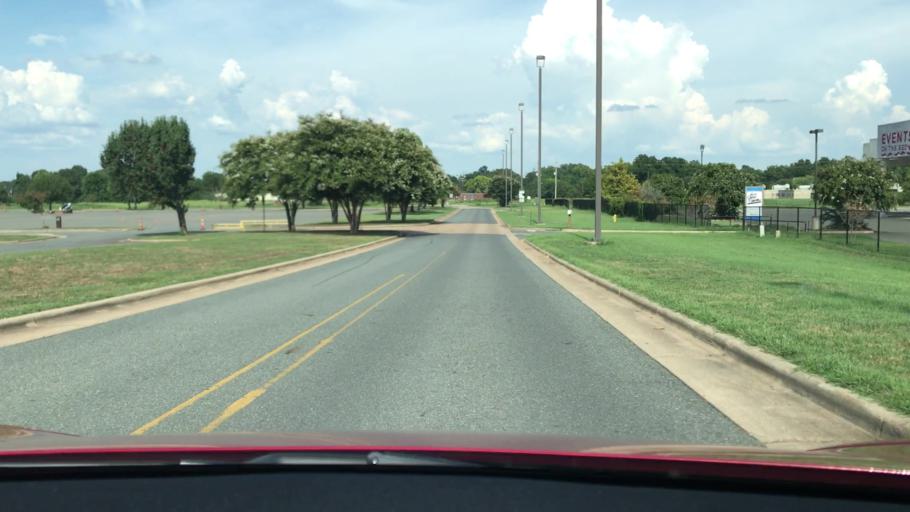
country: US
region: Louisiana
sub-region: Bossier Parish
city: Bossier City
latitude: 32.4623
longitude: -93.6745
